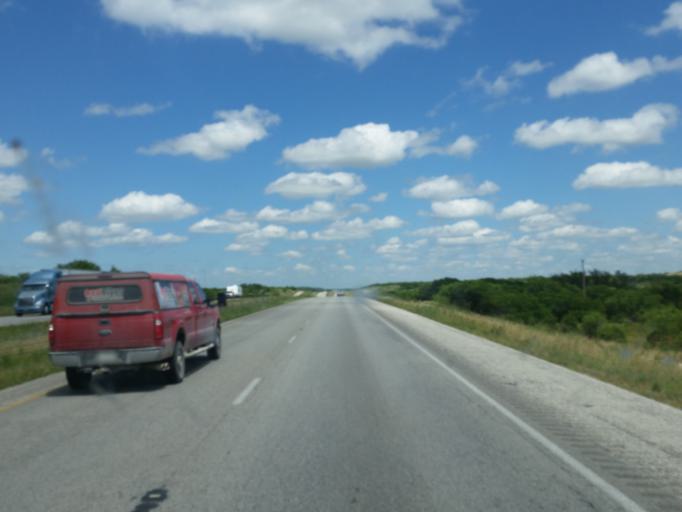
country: US
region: Texas
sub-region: Callahan County
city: Baird
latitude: 32.3826
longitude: -99.2794
